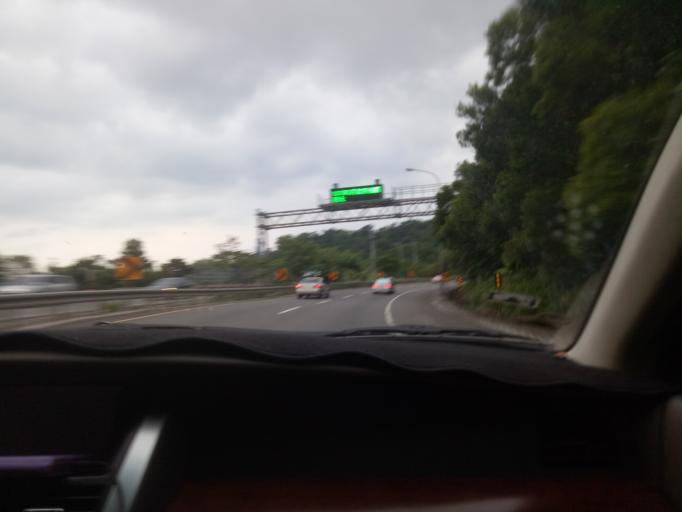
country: TW
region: Taiwan
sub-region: Keelung
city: Keelung
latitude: 25.1068
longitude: 121.7610
